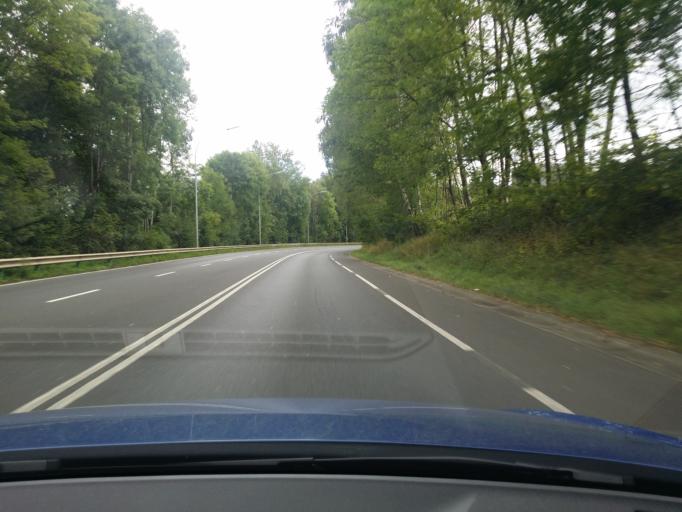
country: LU
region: Luxembourg
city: Kirchberg
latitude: 49.6149
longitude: 6.1679
